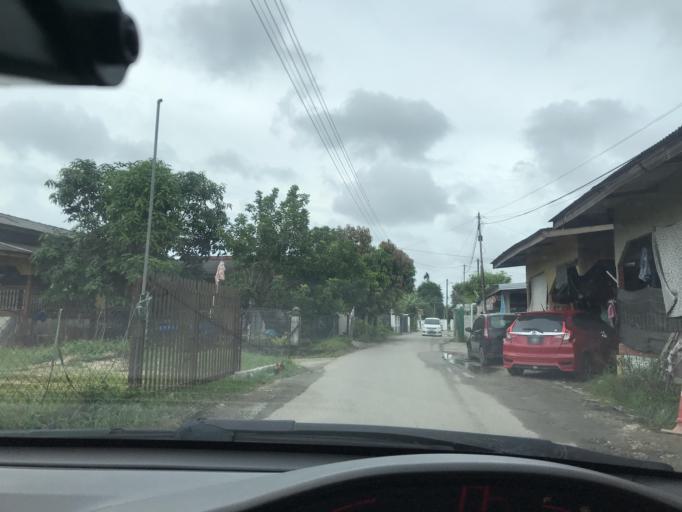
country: MY
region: Kelantan
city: Kota Bharu
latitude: 6.1137
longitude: 102.2187
